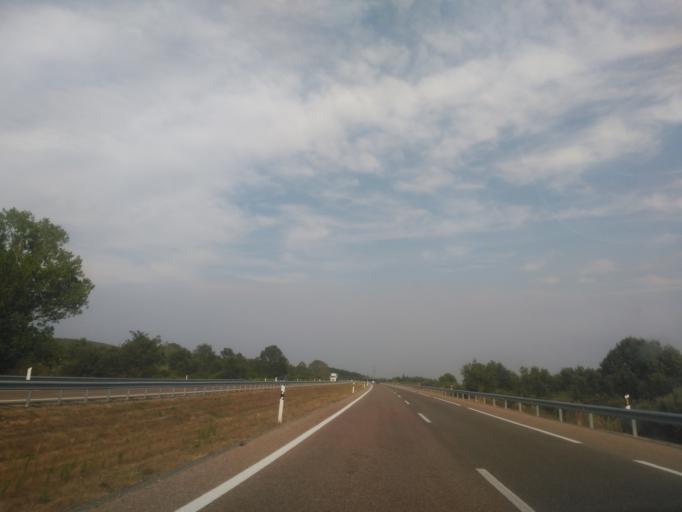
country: ES
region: Castille and Leon
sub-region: Provincia de Zamora
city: Asturianos
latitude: 42.0435
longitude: -6.4824
